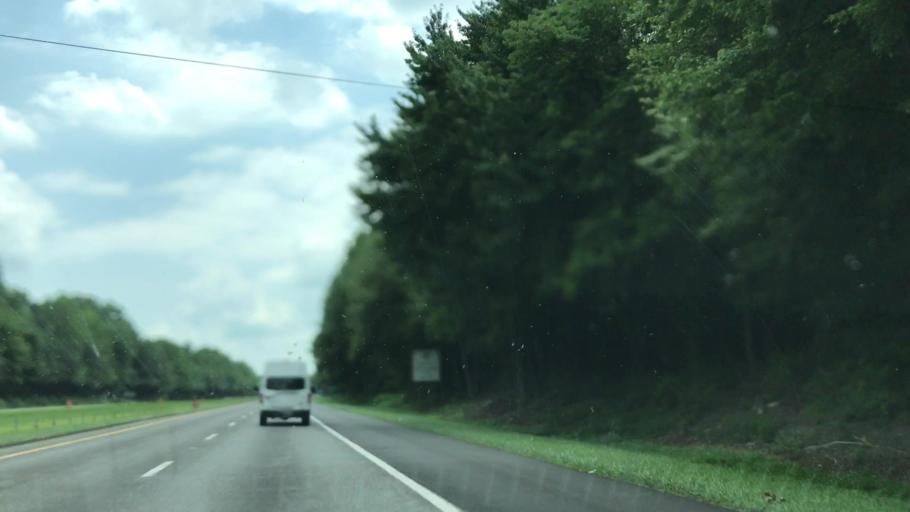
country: US
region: North Carolina
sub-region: Surry County
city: Dobson
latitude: 36.4103
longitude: -80.7814
